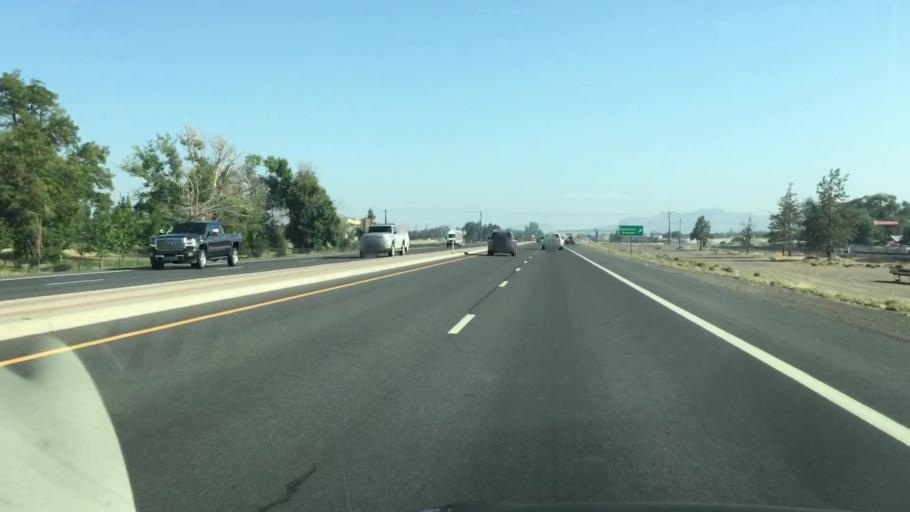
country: US
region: Oregon
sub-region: Deschutes County
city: Redmond
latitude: 44.2809
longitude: -121.1685
